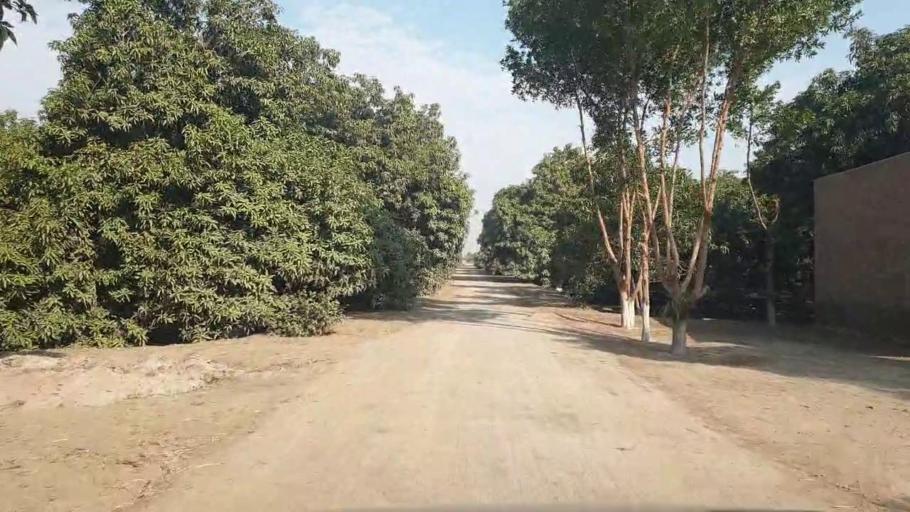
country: PK
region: Sindh
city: Tando Adam
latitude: 25.7548
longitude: 68.5882
